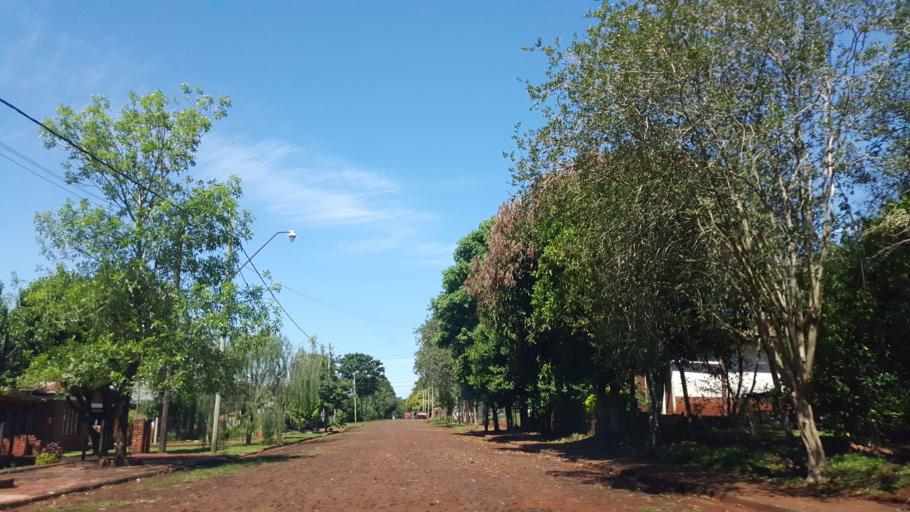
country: AR
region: Misiones
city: Capiovi
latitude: -26.9310
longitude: -55.0649
